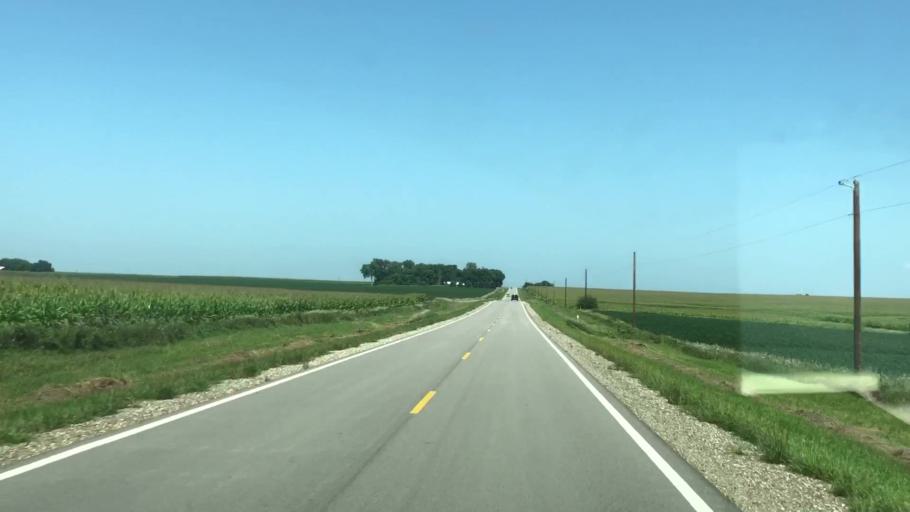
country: US
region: Iowa
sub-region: O'Brien County
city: Sanborn
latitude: 43.2640
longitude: -95.7236
